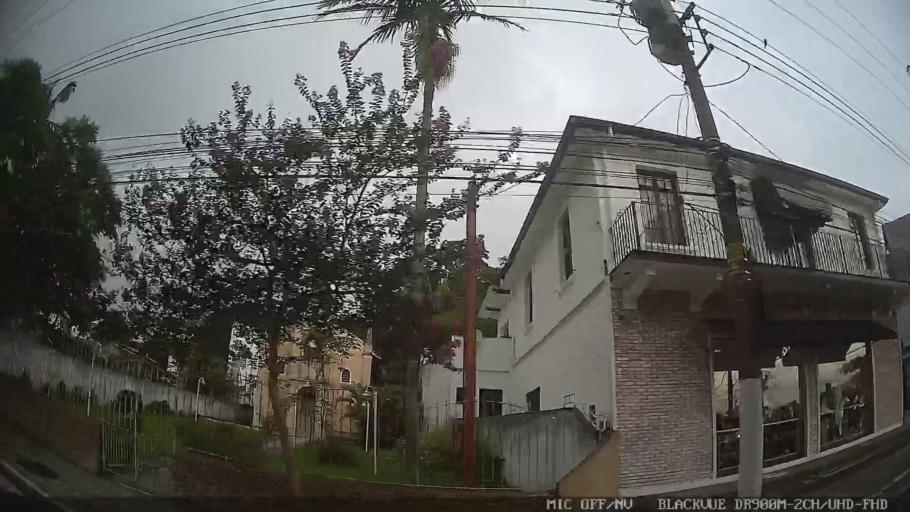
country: BR
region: Sao Paulo
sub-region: Ribeirao Pires
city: Ribeirao Pires
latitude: -23.7106
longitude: -46.4109
